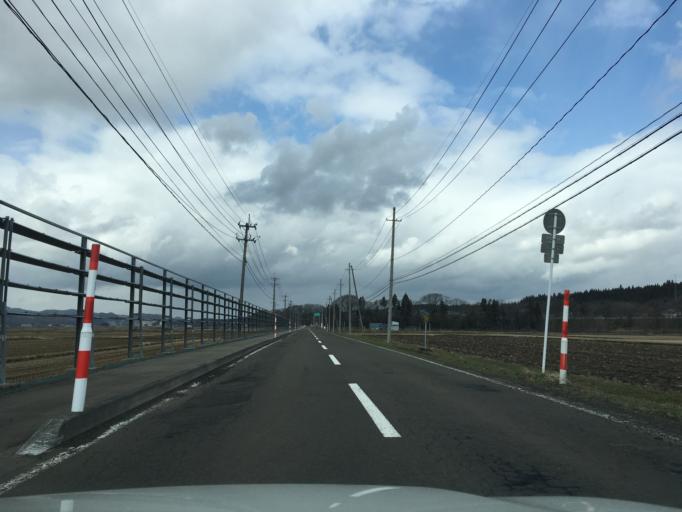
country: JP
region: Akita
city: Takanosu
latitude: 40.1389
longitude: 140.3517
